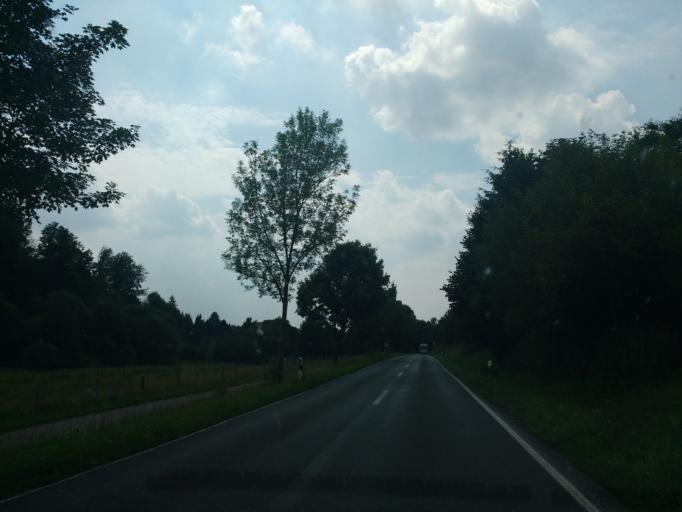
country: DE
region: North Rhine-Westphalia
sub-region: Regierungsbezirk Detmold
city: Dorentrup
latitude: 52.0451
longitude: 9.0182
